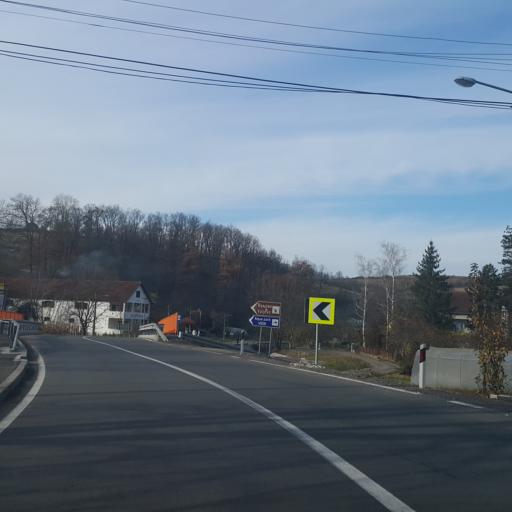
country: RS
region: Central Serbia
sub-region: Belgrade
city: Lazarevac
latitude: 44.3485
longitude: 20.4001
